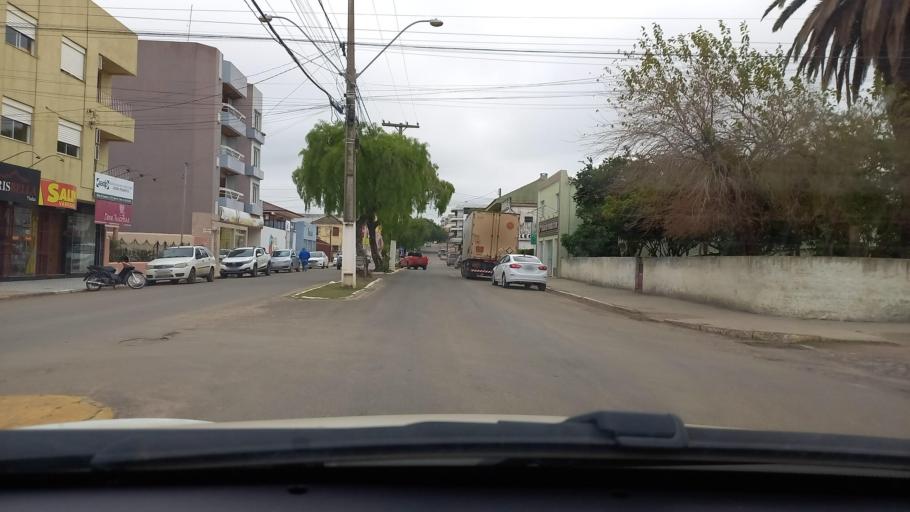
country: BR
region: Rio Grande do Sul
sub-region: Dom Pedrito
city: Dom Pedrito
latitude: -30.9779
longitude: -54.6738
